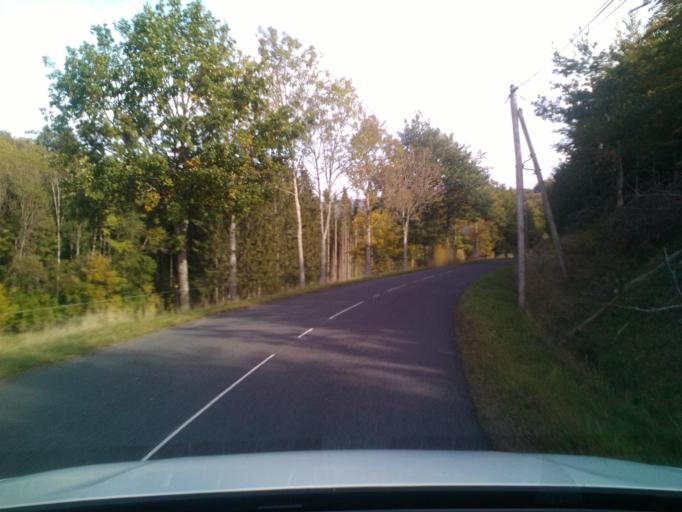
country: FR
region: Lorraine
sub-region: Departement des Vosges
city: Senones
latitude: 48.3604
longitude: 7.0251
